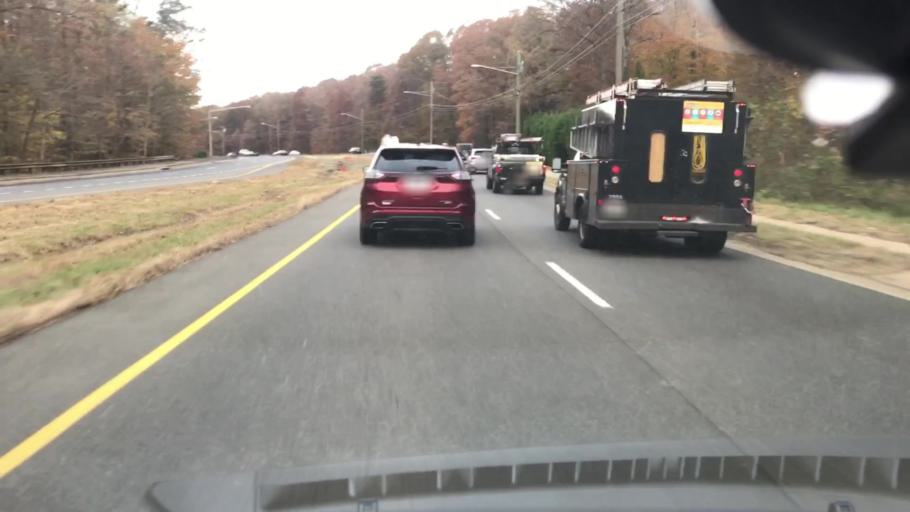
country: US
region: Virginia
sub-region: City of Fairfax
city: Fairfax
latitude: 38.8330
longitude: -77.3363
